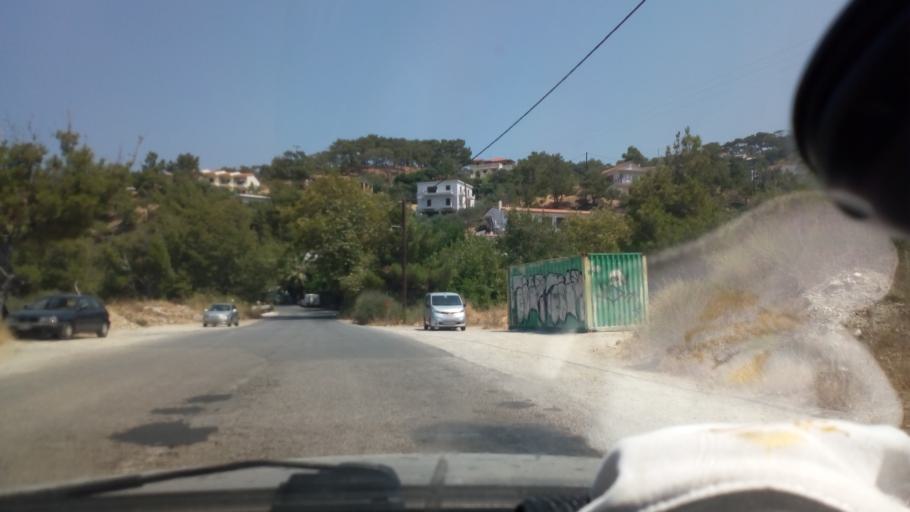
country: GR
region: North Aegean
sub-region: Nomos Samou
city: Agios Kirykos
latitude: 37.6291
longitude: 26.1015
